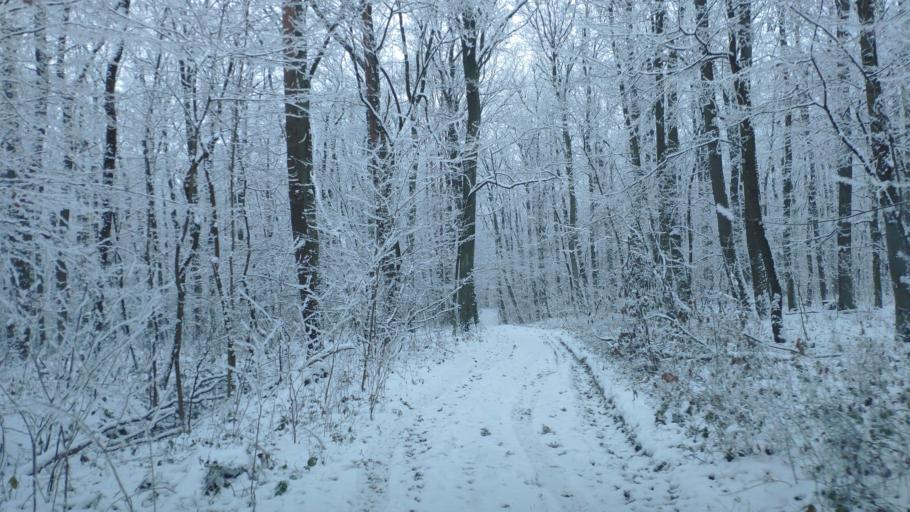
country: SK
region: Kosicky
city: Kosice
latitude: 48.6452
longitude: 21.1811
